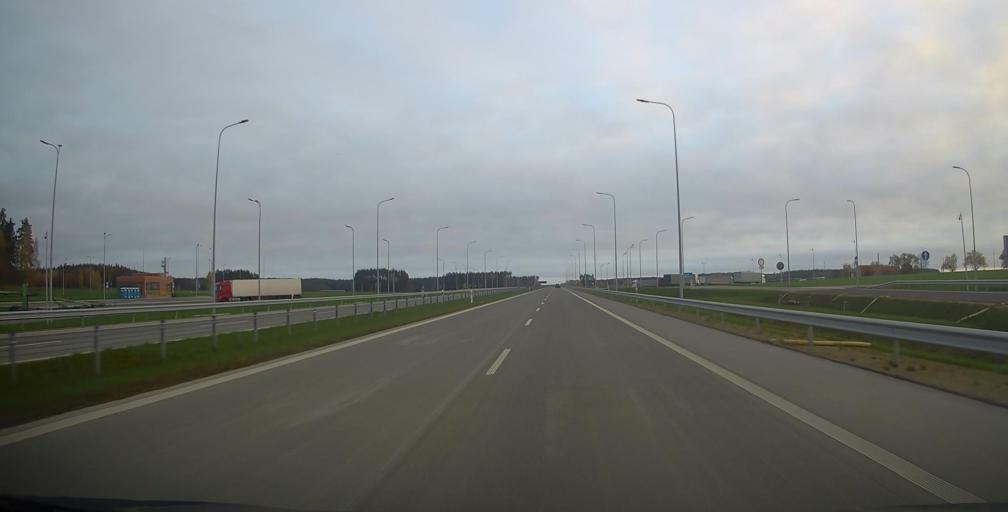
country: PL
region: Podlasie
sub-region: Powiat lomzynski
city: Piatnica
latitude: 53.2696
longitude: 22.1249
